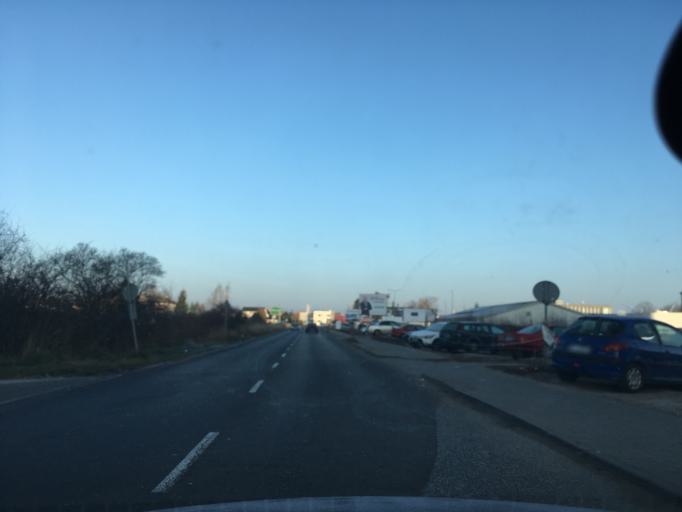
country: PL
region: Masovian Voivodeship
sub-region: Powiat piaseczynski
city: Piaseczno
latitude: 52.0803
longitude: 21.0085
